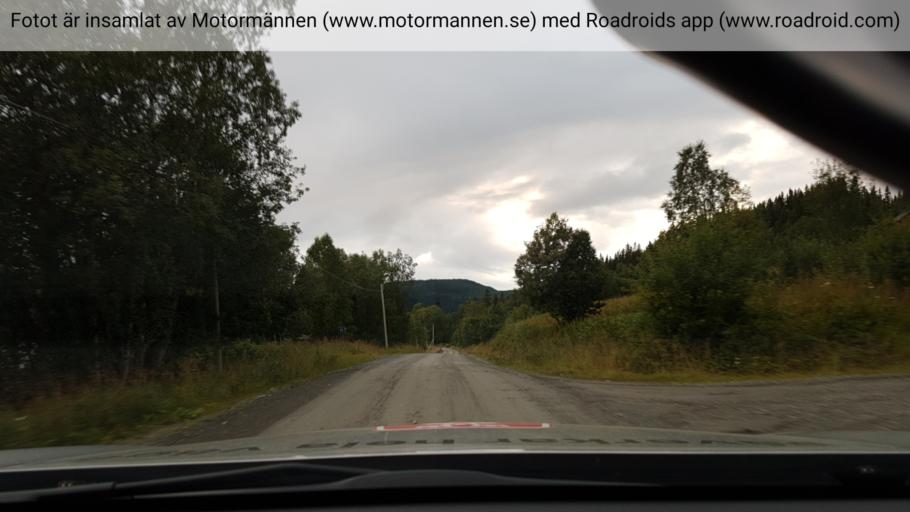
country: NO
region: Nordland
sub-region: Hattfjelldal
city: Hattfjelldal
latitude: 65.6527
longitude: 15.1658
